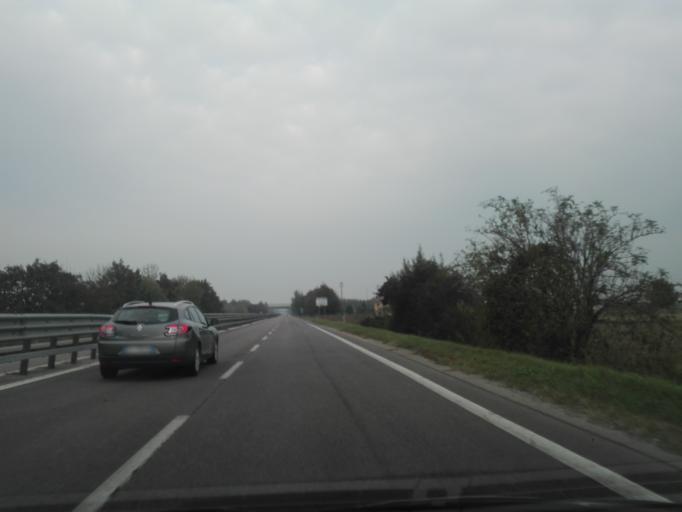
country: IT
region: Veneto
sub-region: Provincia di Verona
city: Spinimbecco
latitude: 45.1354
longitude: 11.3648
